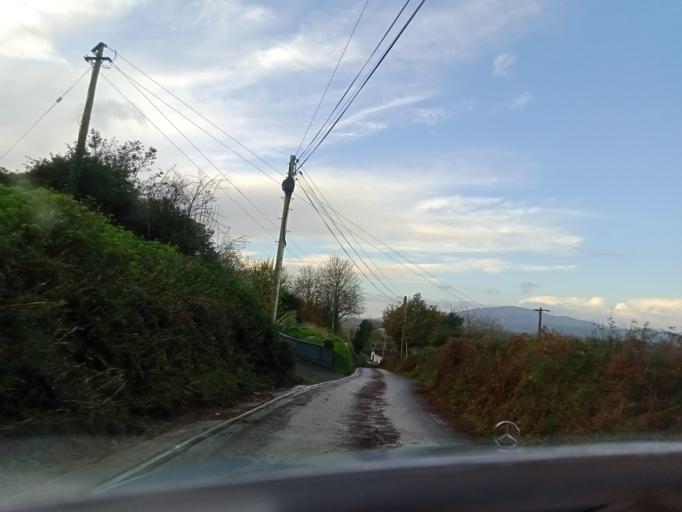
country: IE
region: Munster
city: Carrick-on-Suir
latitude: 52.3383
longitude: -7.4124
